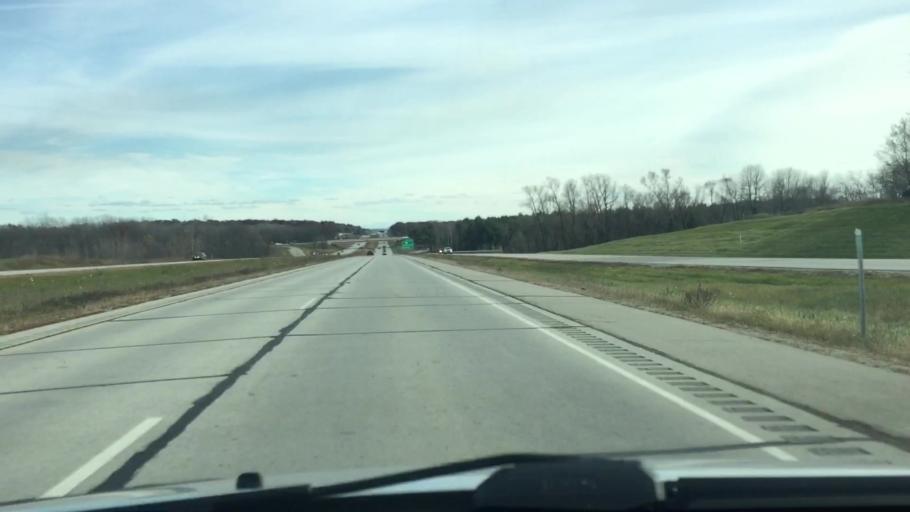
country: US
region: Wisconsin
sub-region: Brown County
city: Howard
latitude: 44.5641
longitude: -88.1395
